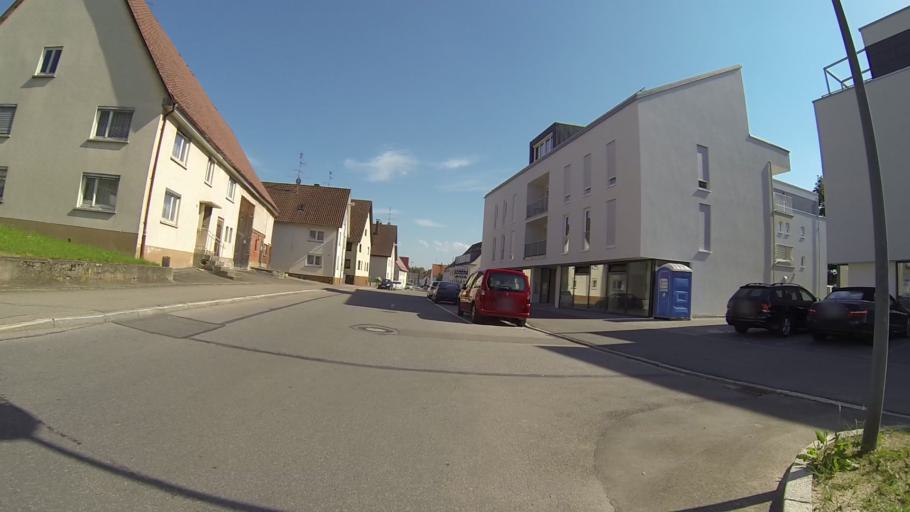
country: DE
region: Baden-Wuerttemberg
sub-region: Tuebingen Region
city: Laupheim
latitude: 48.2275
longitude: 9.8856
